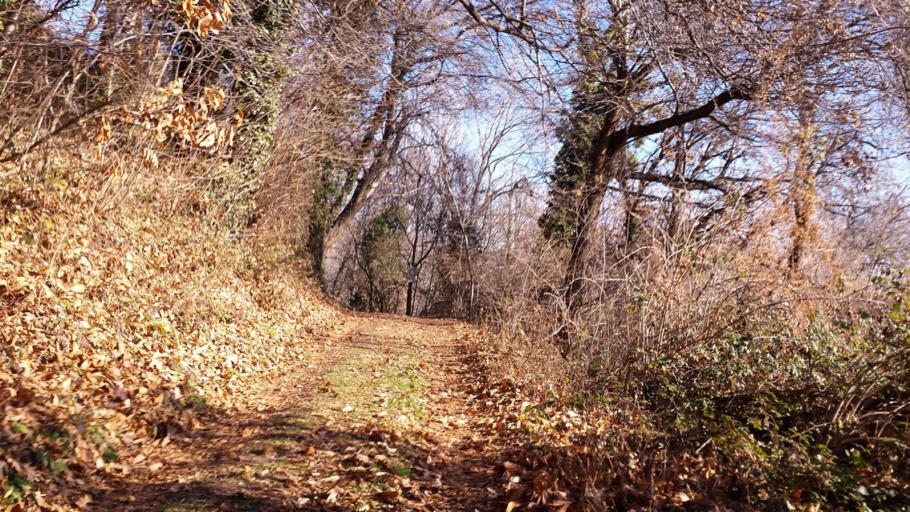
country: IT
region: Veneto
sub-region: Provincia di Treviso
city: Paderno del Grappa
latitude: 45.8371
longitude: 11.8682
